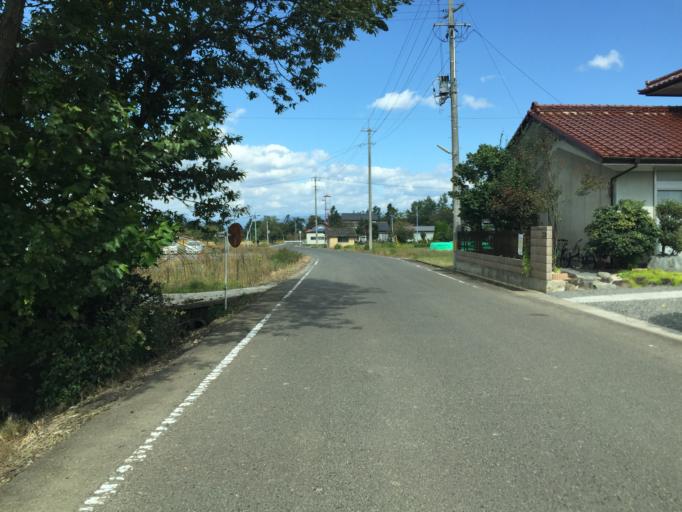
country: JP
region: Fukushima
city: Fukushima-shi
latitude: 37.7054
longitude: 140.4496
